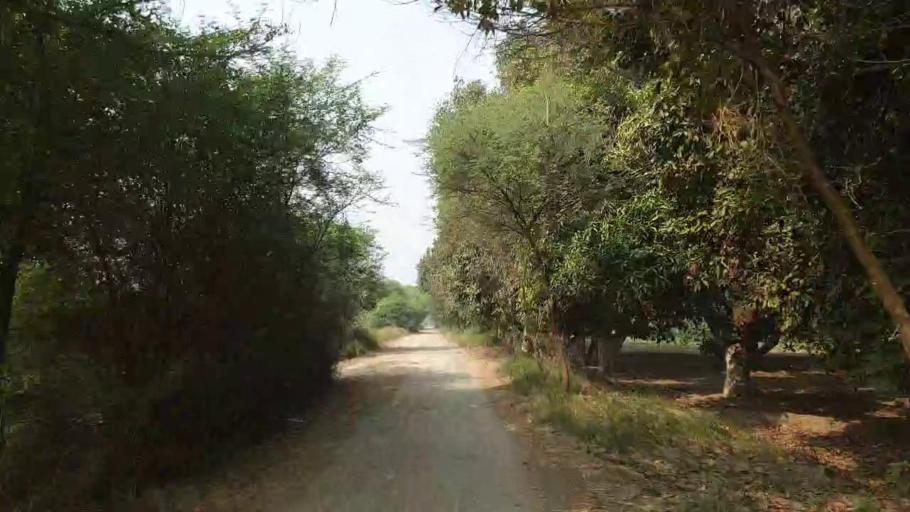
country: PK
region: Sindh
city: Tando Muhammad Khan
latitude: 25.2173
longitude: 68.5547
